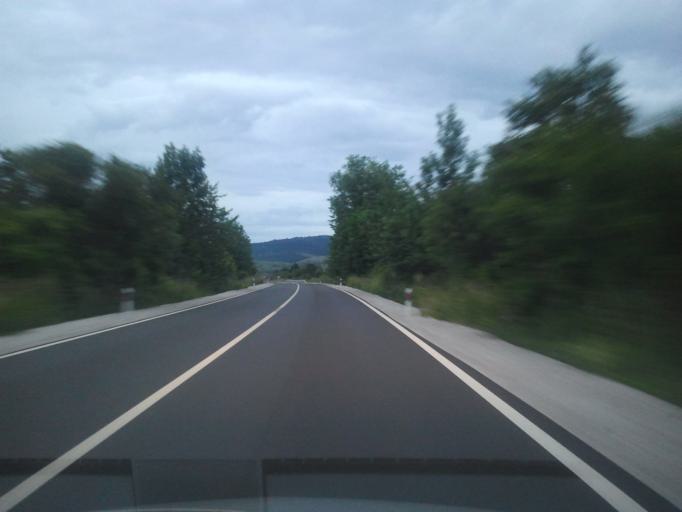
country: HR
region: Zadarska
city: Gracac
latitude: 44.3450
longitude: 15.8671
